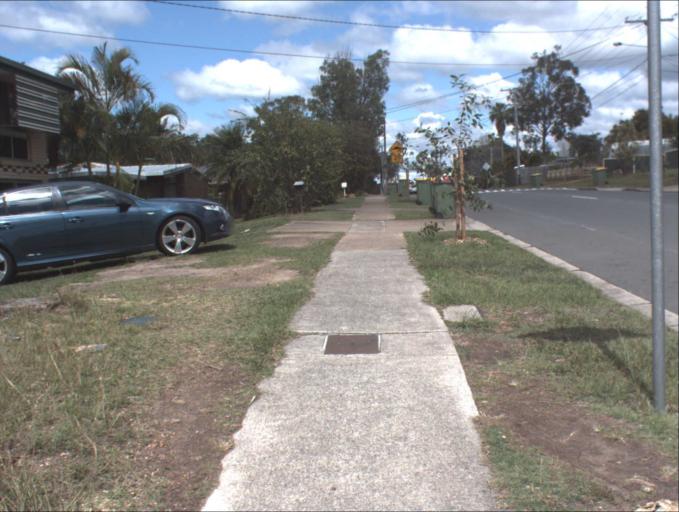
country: AU
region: Queensland
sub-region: Brisbane
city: Sunnybank Hills
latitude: -27.6630
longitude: 153.0294
